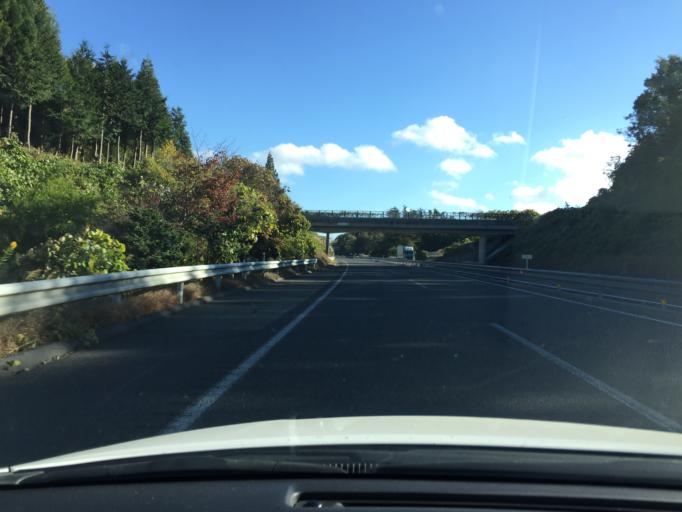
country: JP
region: Fukushima
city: Funehikimachi-funehiki
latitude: 37.4153
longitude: 140.5620
